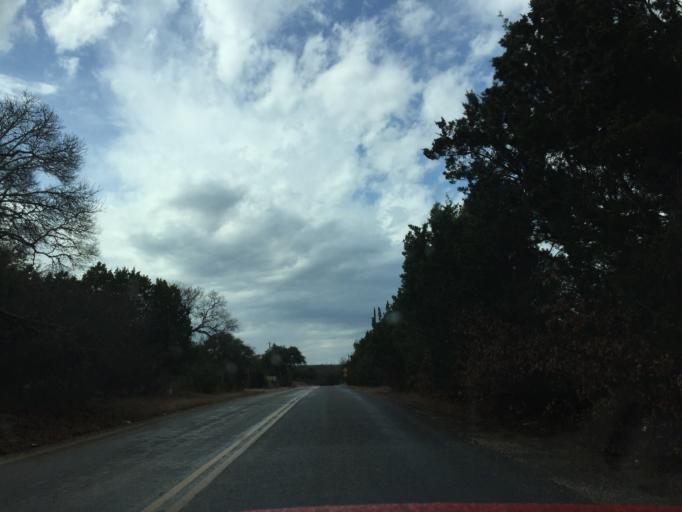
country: US
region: Texas
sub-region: Williamson County
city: Leander
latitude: 30.6306
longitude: -97.9741
